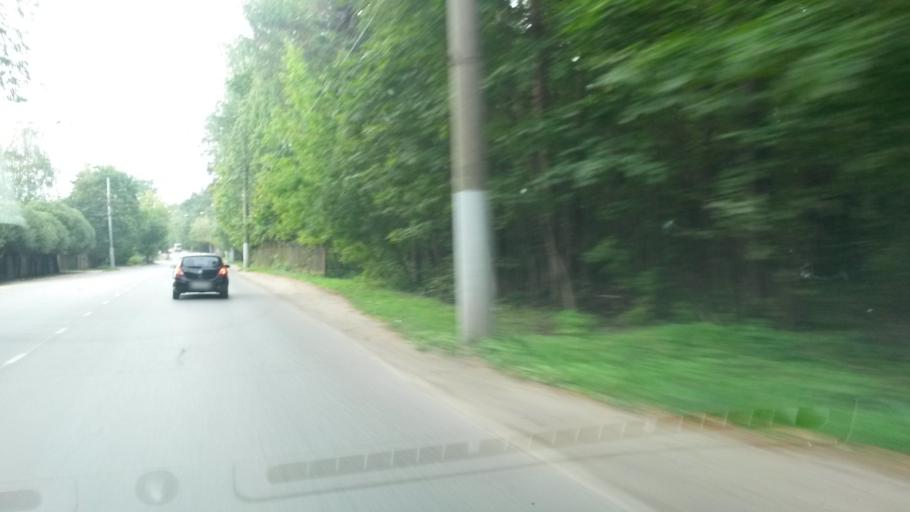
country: RU
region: Ivanovo
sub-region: Gorod Ivanovo
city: Ivanovo
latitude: 57.0243
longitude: 40.9424
